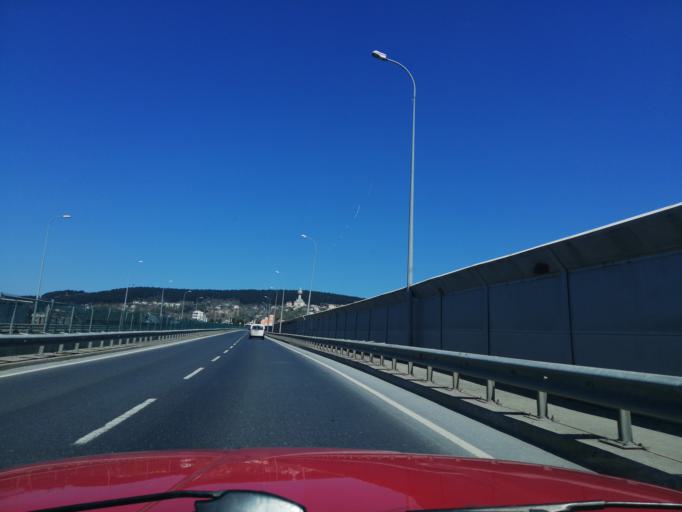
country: TR
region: Istanbul
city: Mahmut Sevket Pasa
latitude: 41.1134
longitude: 29.1190
